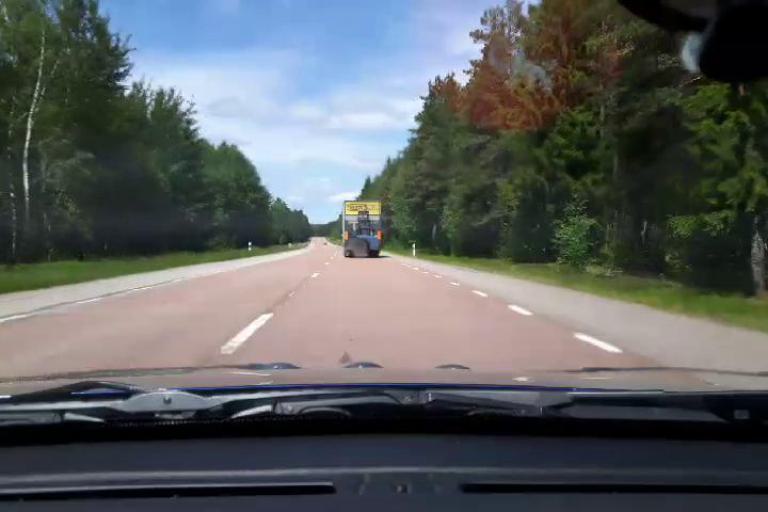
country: SE
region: Uppsala
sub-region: Osthammars Kommun
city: Bjorklinge
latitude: 60.1327
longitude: 17.5088
